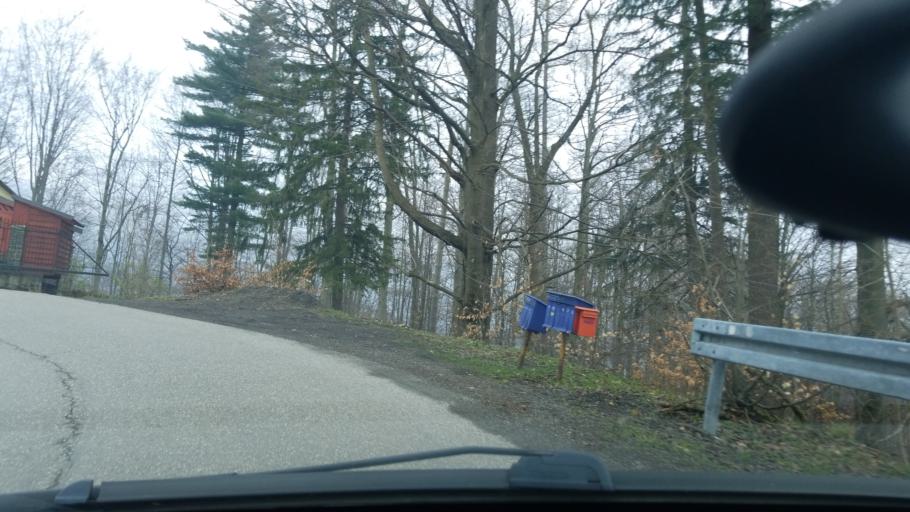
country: PL
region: Silesian Voivodeship
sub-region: Powiat cieszynski
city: Ustron
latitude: 49.7138
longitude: 18.8511
